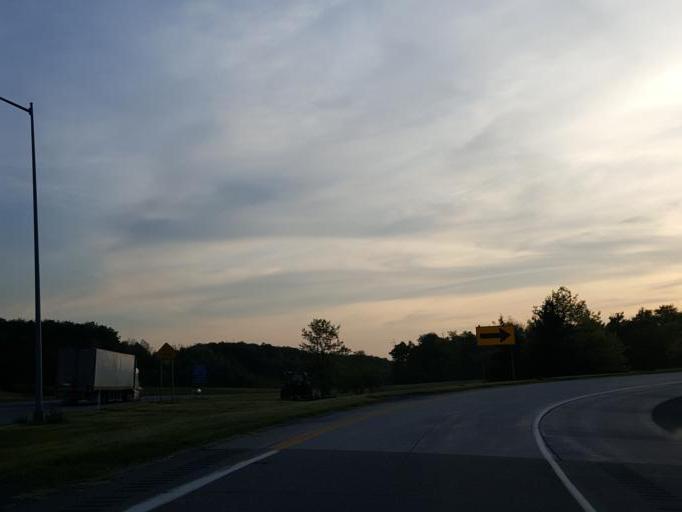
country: US
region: Pennsylvania
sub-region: Cambria County
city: Gallitzin
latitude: 40.4676
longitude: -78.5438
